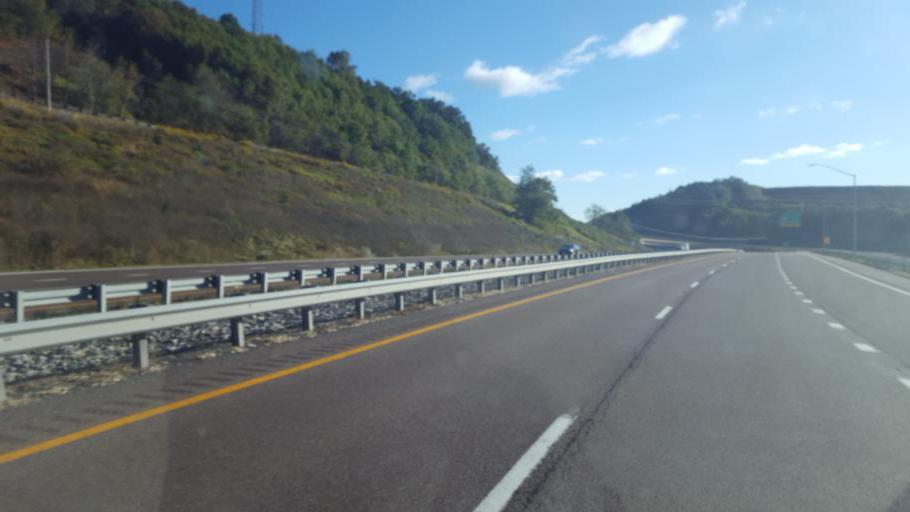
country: US
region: Maryland
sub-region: Allegany County
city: Cumberland
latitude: 39.7046
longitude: -78.6282
